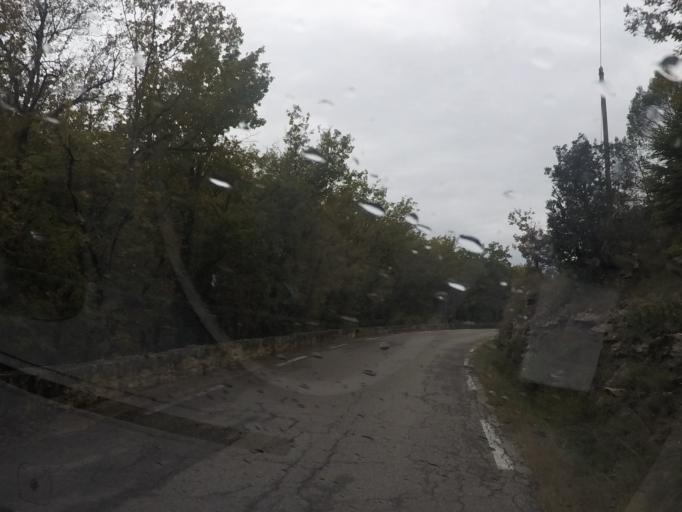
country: FR
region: Provence-Alpes-Cote d'Azur
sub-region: Departement du Vaucluse
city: Bonnieux
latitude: 43.8139
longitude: 5.3306
